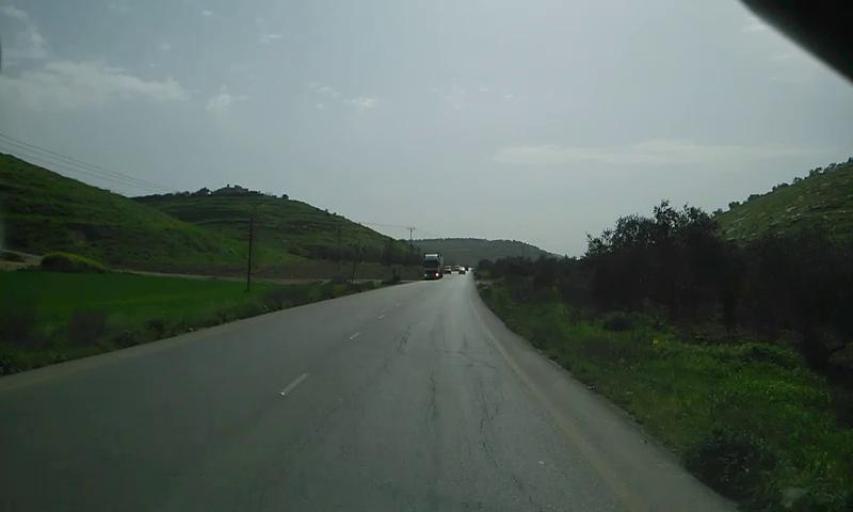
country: PS
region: West Bank
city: Mirkah
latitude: 32.3914
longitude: 35.2185
